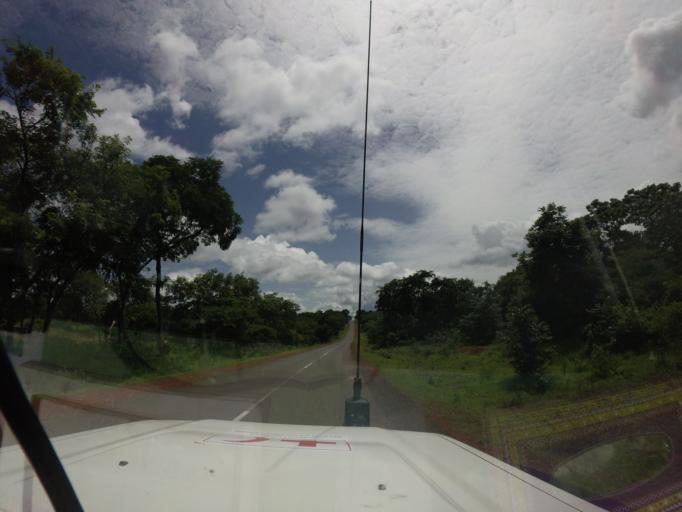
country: SL
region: Northern Province
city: Gberia Fotombu
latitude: 10.1737
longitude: -11.2178
